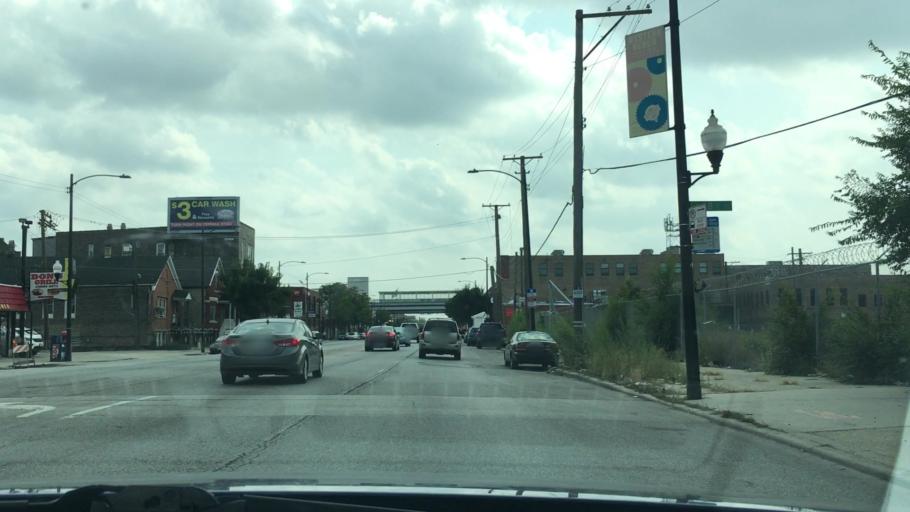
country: US
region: Illinois
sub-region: Cook County
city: Chicago
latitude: 41.8568
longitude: -87.6858
